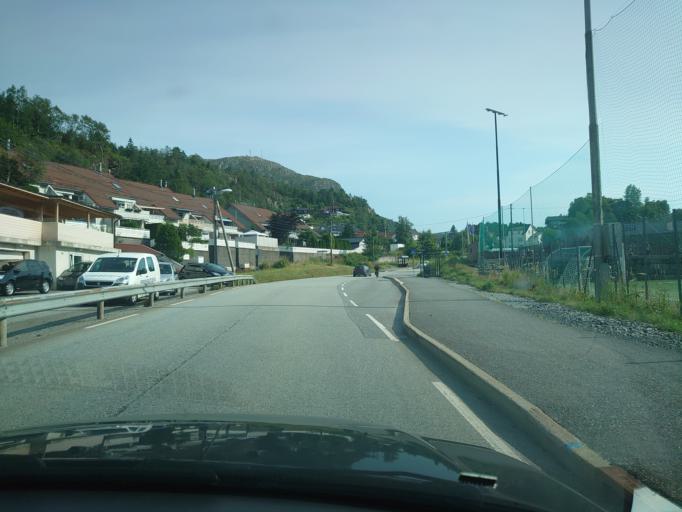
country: NO
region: Hordaland
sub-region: Bergen
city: Bergen
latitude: 60.3707
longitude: 5.3036
